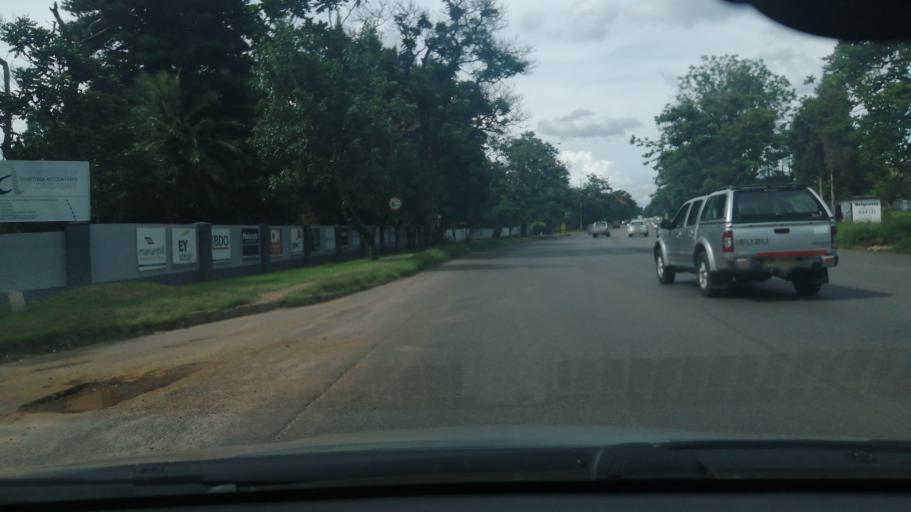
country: ZW
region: Harare
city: Harare
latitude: -17.8020
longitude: 31.0442
